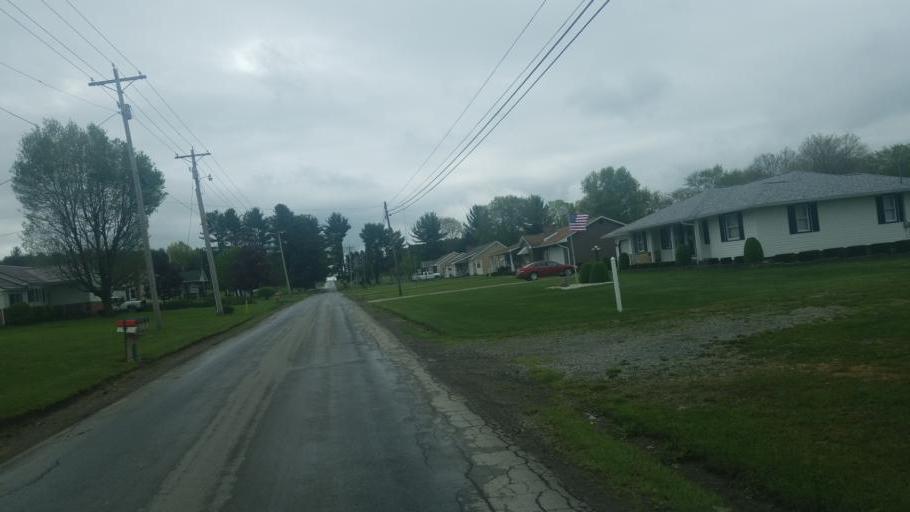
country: US
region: Pennsylvania
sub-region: Forest County
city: Tionesta
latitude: 41.3981
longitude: -79.3880
